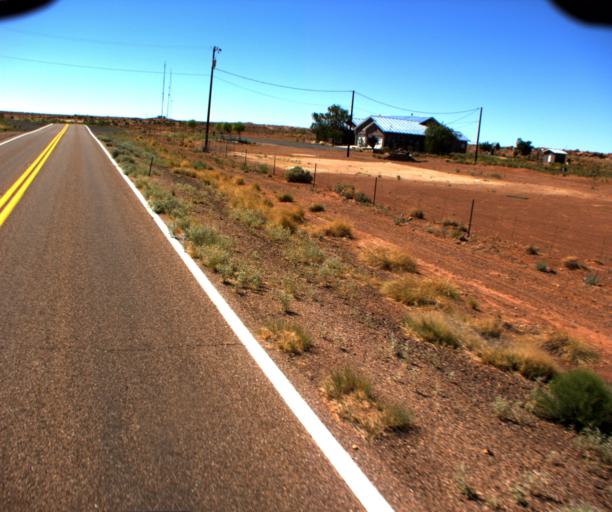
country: US
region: Arizona
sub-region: Navajo County
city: Winslow
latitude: 34.9793
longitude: -110.6576
